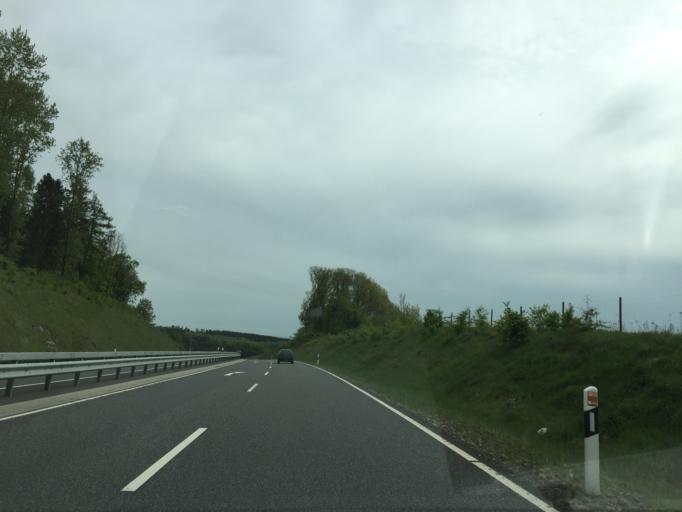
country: DE
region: Rheinland-Pfalz
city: Ettinghausen
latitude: 50.5089
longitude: 7.8770
